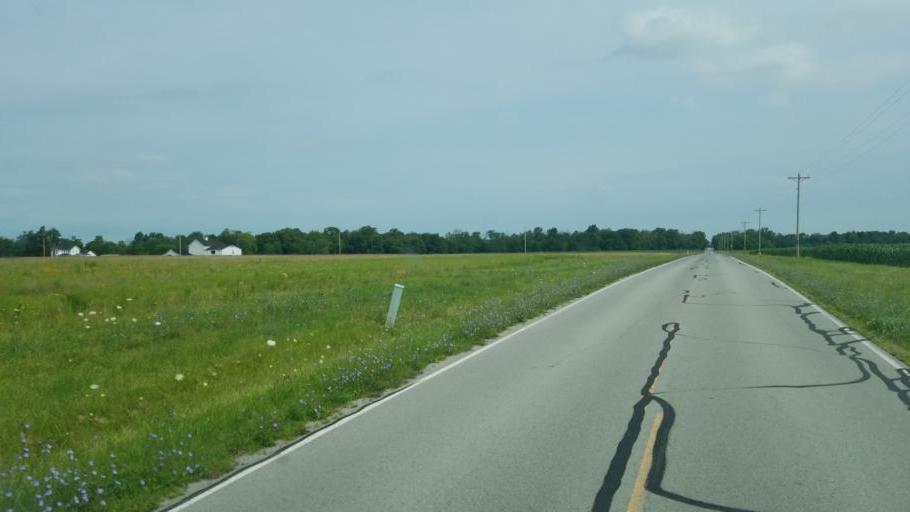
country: US
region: Ohio
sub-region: Wyandot County
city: Carey
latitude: 40.8735
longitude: -83.3807
